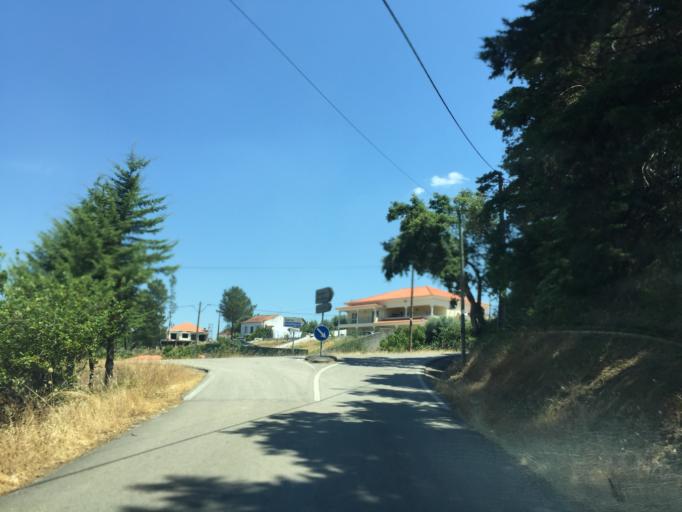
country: PT
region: Santarem
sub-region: Tomar
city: Tomar
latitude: 39.5958
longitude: -8.3302
